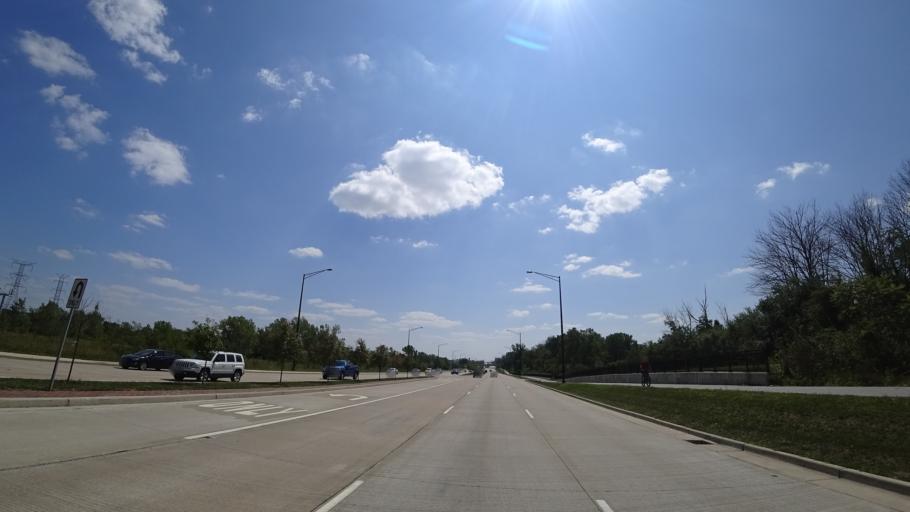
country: US
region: Illinois
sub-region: Cook County
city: Orland Park
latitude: 41.6430
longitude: -87.8540
